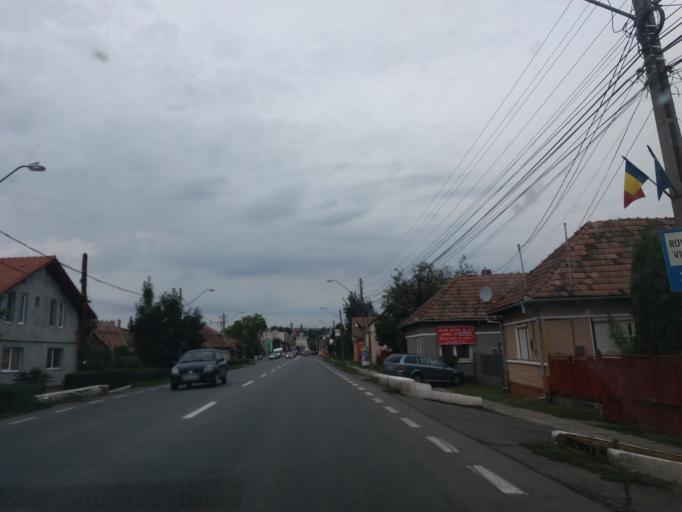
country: RO
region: Mures
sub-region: Municipiul Reghin
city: Reghin
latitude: 46.7689
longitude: 24.7040
